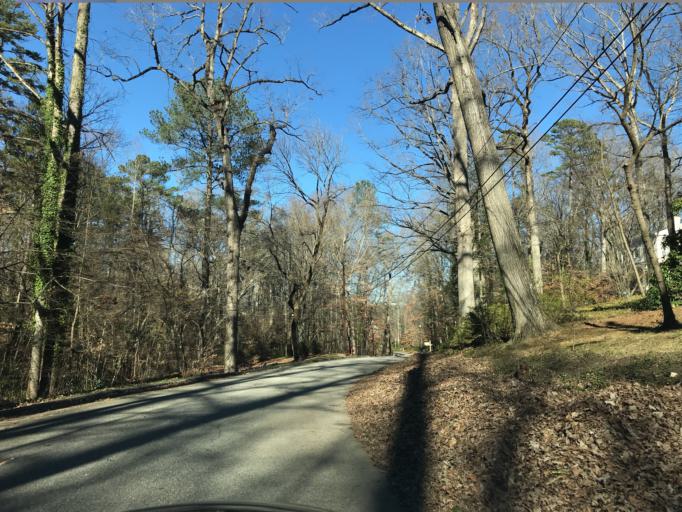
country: US
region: North Carolina
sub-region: Wake County
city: West Raleigh
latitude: 35.8160
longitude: -78.6457
